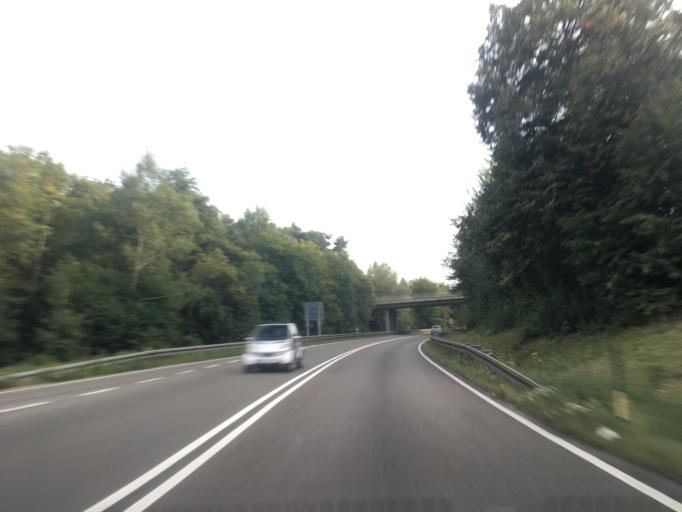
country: DE
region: Baden-Wuerttemberg
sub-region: Tuebingen Region
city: Metzingen
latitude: 48.5429
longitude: 9.2684
